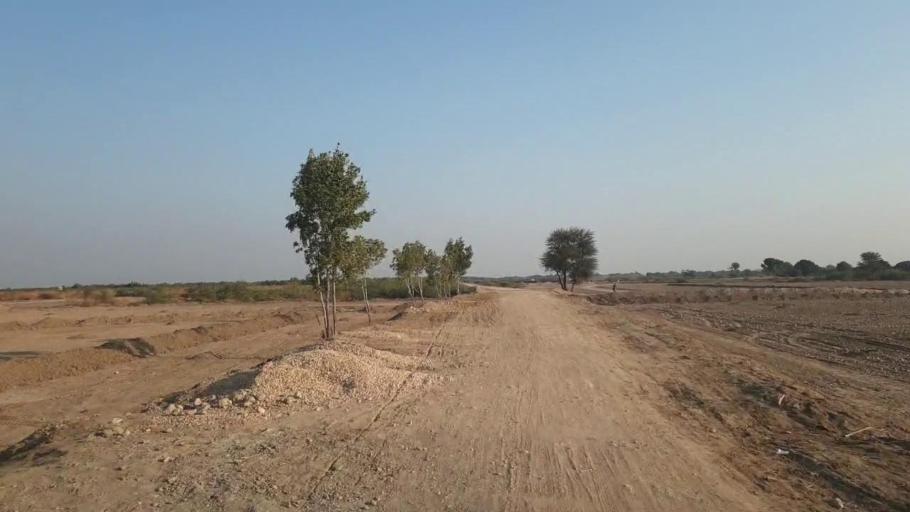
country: PK
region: Sindh
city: Mirpur Khas
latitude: 25.4271
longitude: 68.9010
